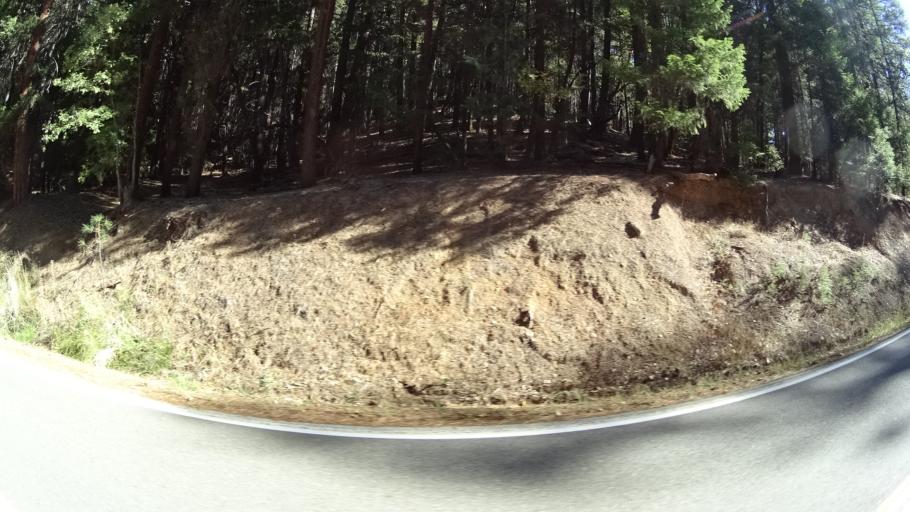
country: US
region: California
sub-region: Trinity County
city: Weaverville
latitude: 41.2093
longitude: -123.0576
